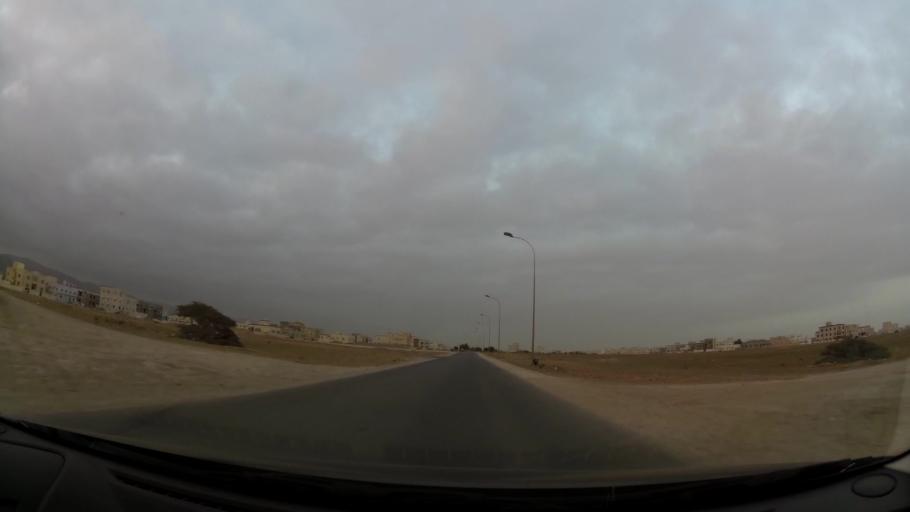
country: OM
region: Zufar
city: Salalah
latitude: 17.0380
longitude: 54.0283
